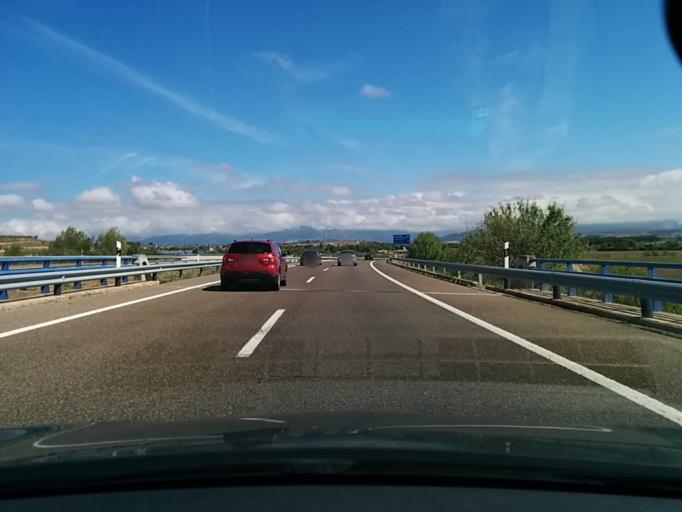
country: ES
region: Aragon
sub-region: Provincia de Huesca
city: Huesca
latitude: 42.1388
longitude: -0.4310
